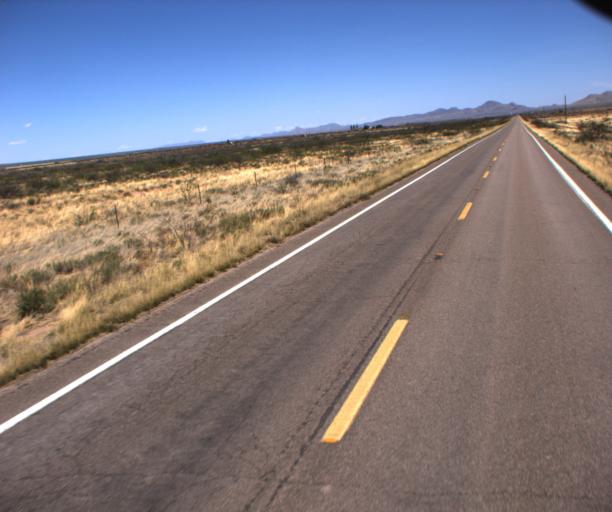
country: US
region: Arizona
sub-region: Cochise County
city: Douglas
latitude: 31.7828
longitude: -109.0686
